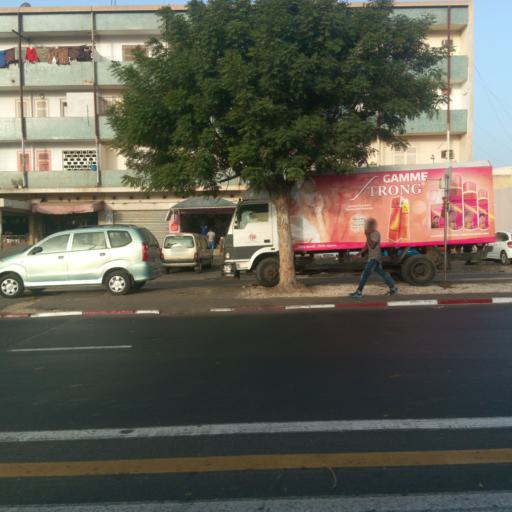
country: SN
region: Dakar
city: Dakar
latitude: 14.6839
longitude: -17.4447
